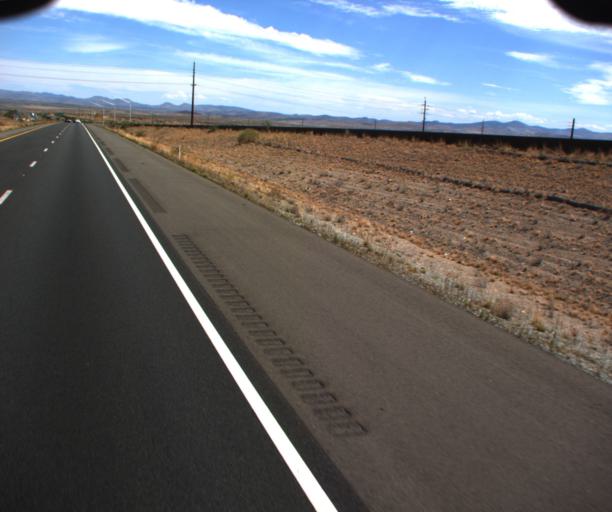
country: US
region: Arizona
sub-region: Yavapai County
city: Cordes Lakes
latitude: 34.3353
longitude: -112.1193
